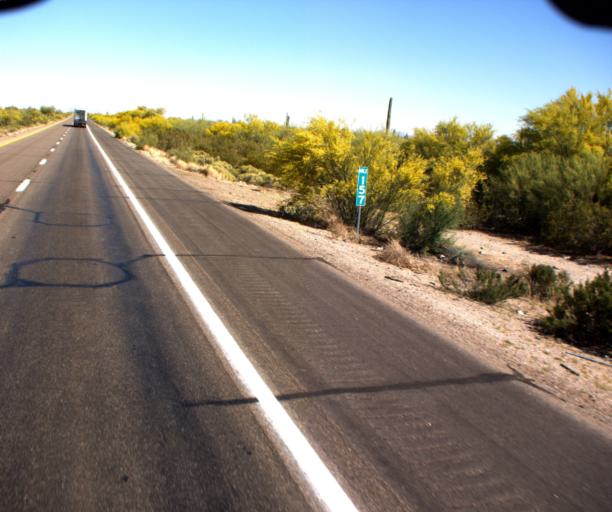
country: US
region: Arizona
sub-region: Pinal County
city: Maricopa
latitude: 32.8307
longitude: -112.0423
